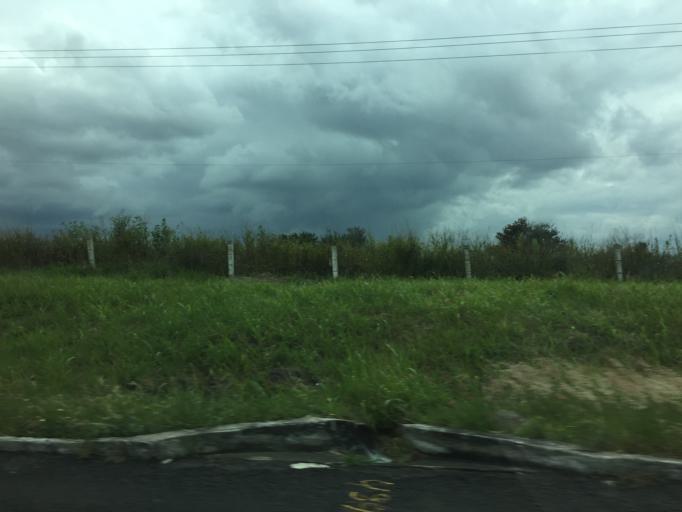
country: MX
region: Jalisco
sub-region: Zapotlanejo
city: La Mezquitera
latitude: 20.5929
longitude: -103.1077
